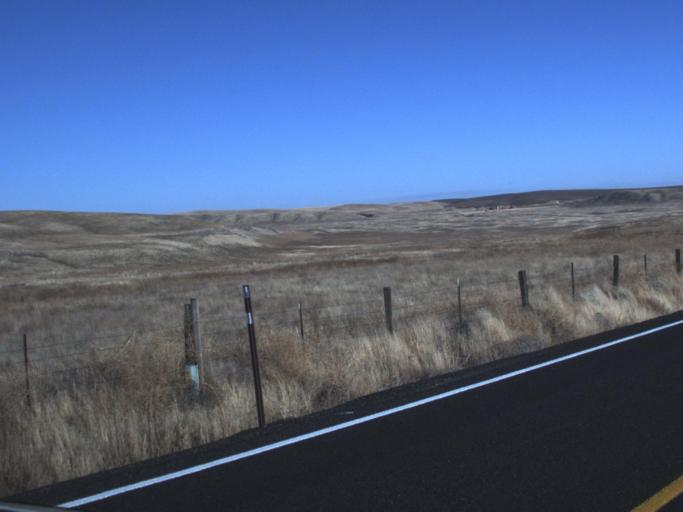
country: US
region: Washington
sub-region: Adams County
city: Ritzville
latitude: 46.8212
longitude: -118.3195
